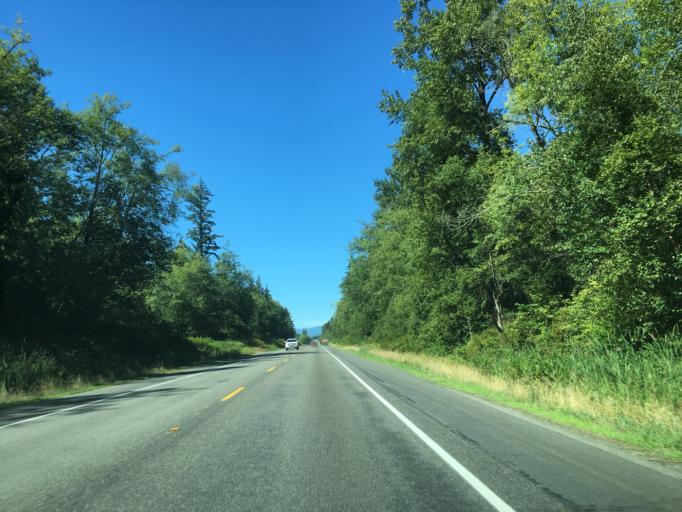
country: US
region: Washington
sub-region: Snohomish County
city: Sisco Heights
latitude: 48.1336
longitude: -122.1128
